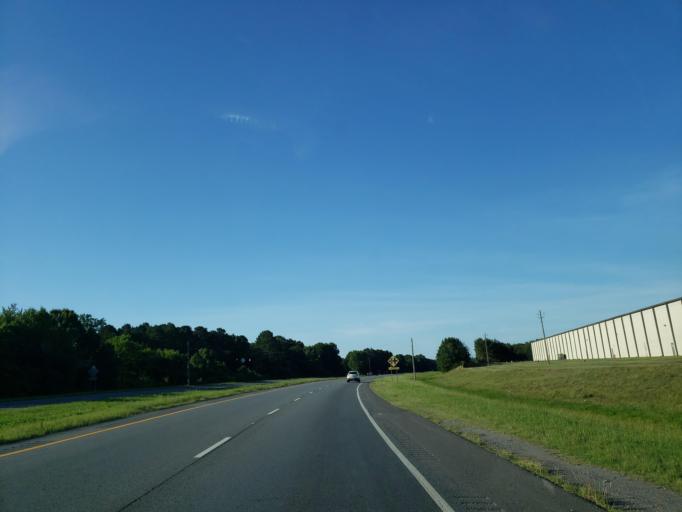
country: US
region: Georgia
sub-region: Floyd County
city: Shannon
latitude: 34.3441
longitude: -85.0776
